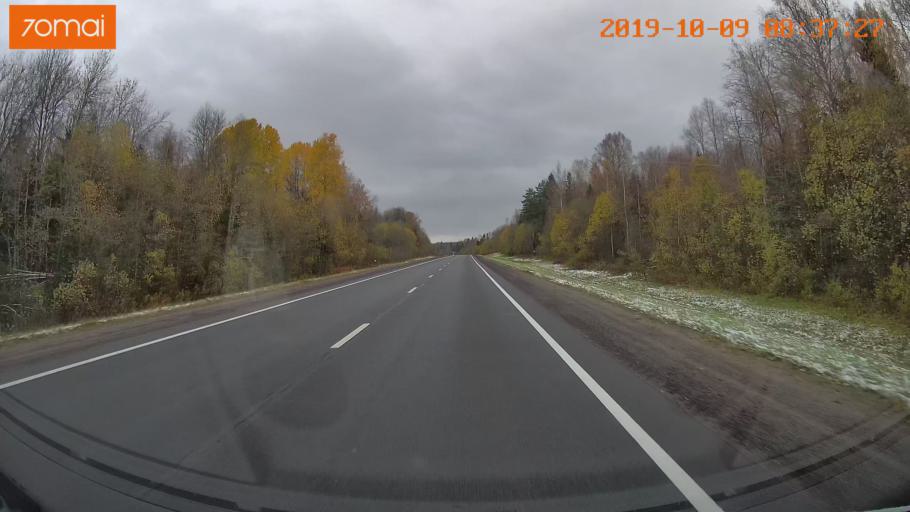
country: RU
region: Vologda
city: Gryazovets
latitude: 58.9416
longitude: 40.1744
